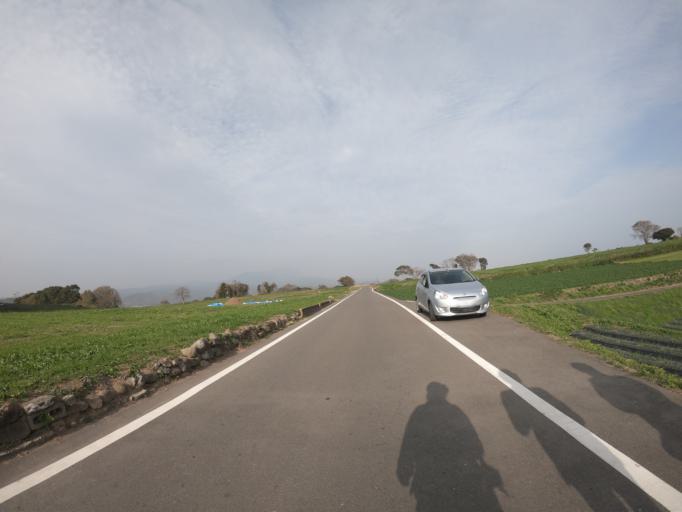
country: JP
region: Nagasaki
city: Shimabara
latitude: 32.6312
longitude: 130.2546
